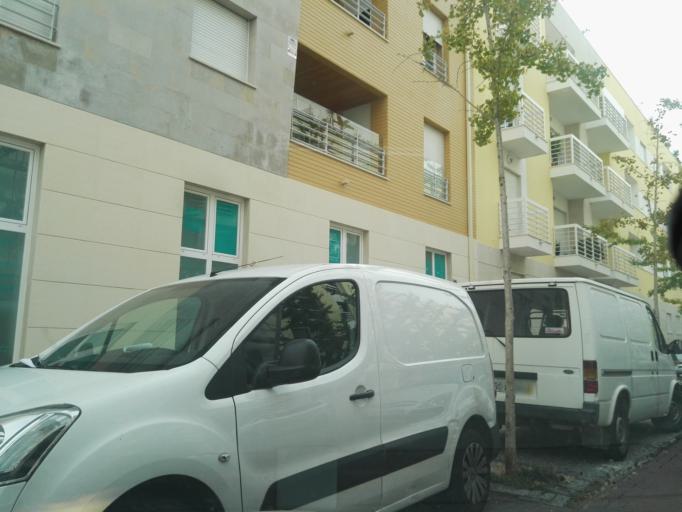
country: PT
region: Lisbon
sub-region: Loures
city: Moscavide
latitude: 38.7585
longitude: -9.0952
